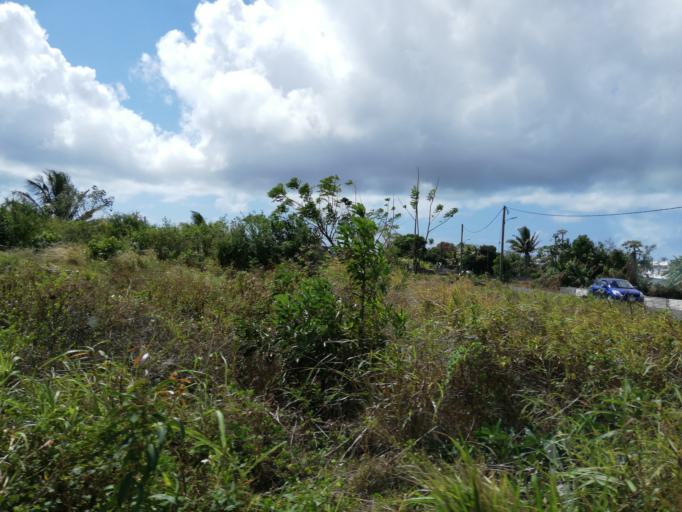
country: MU
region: Riviere du Rempart
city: Esperance Trebuchet
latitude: -20.0736
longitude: 57.6448
